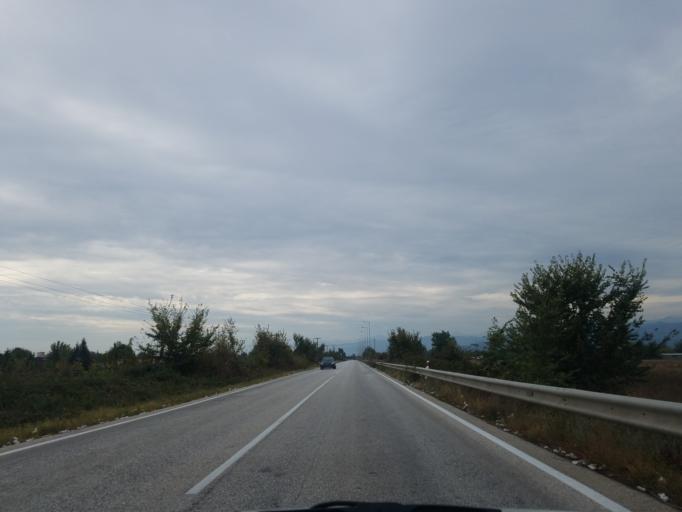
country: GR
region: Thessaly
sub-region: Nomos Kardhitsas
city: Agnantero
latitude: 39.4892
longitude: 21.8383
